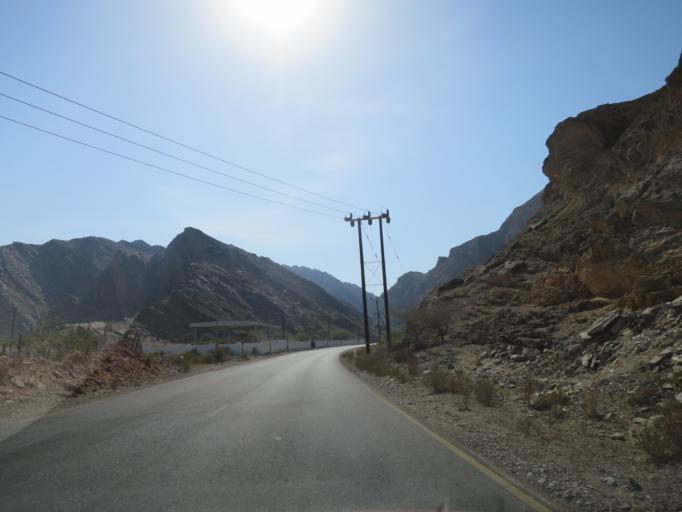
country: OM
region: Muhafazat Masqat
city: Muscat
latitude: 23.5162
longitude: 58.6991
